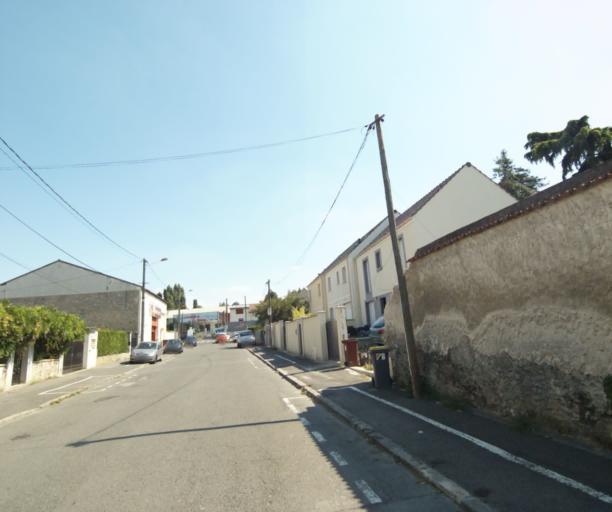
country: FR
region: Ile-de-France
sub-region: Departement de Seine-et-Marne
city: Pomponne
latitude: 48.8754
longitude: 2.6929
